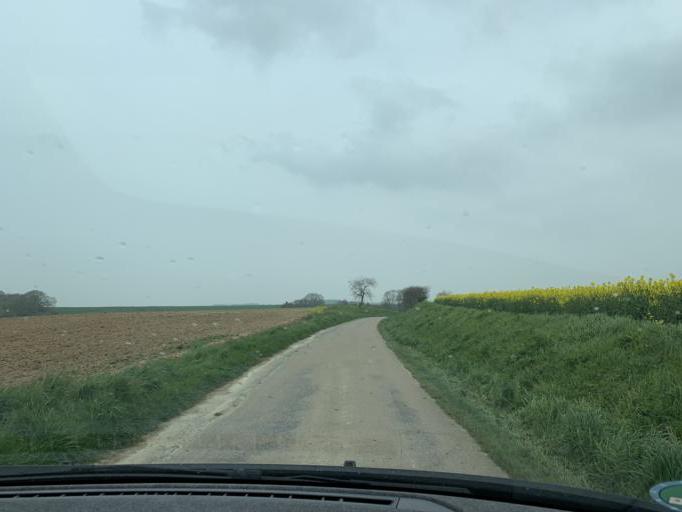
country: FR
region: Haute-Normandie
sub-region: Departement de la Seine-Maritime
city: Fontaine-le-Dun
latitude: 49.8565
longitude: 0.8136
